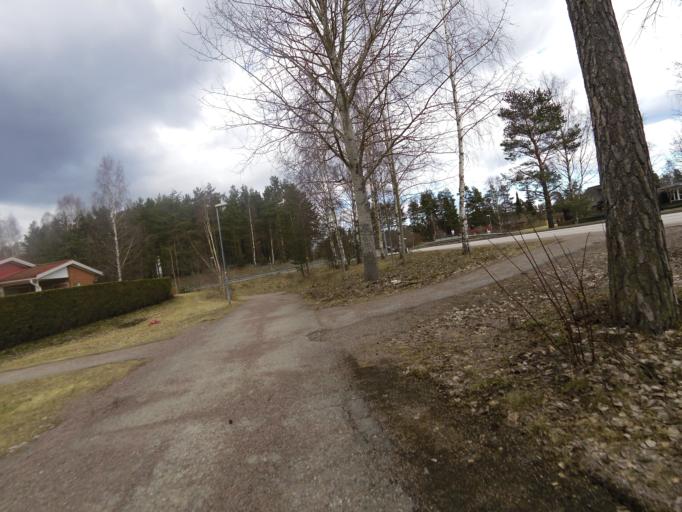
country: SE
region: Gaevleborg
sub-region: Gavle Kommun
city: Gavle
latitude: 60.6908
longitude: 17.0929
